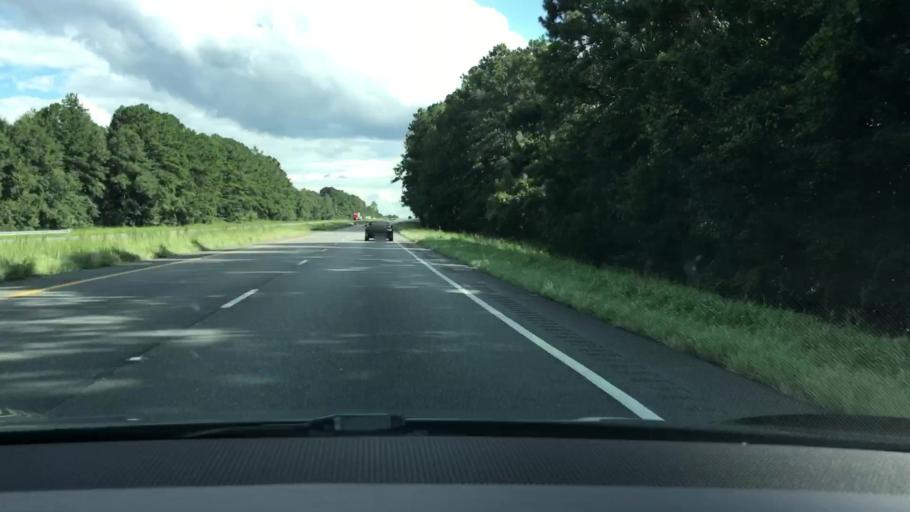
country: US
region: Alabama
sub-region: Pike County
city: Troy
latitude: 31.9096
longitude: -86.0124
